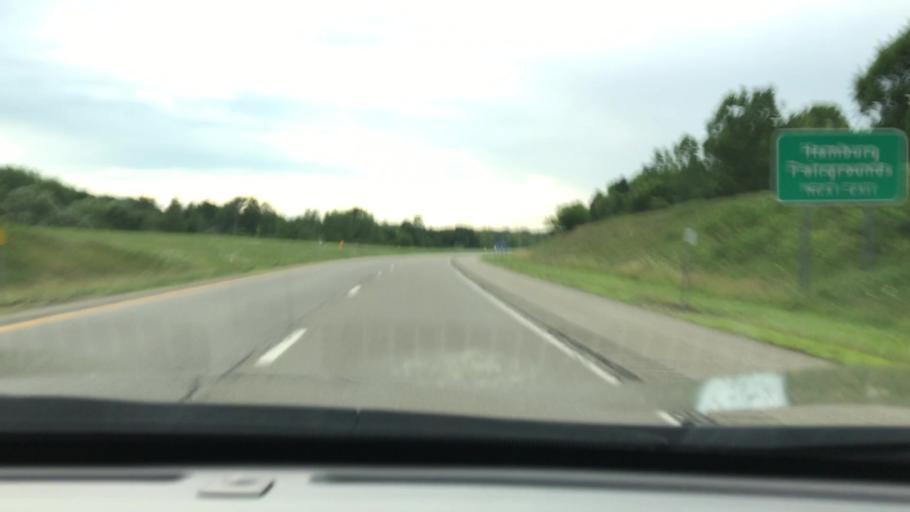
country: US
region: New York
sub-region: Erie County
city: North Boston
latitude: 42.6805
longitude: -78.7856
